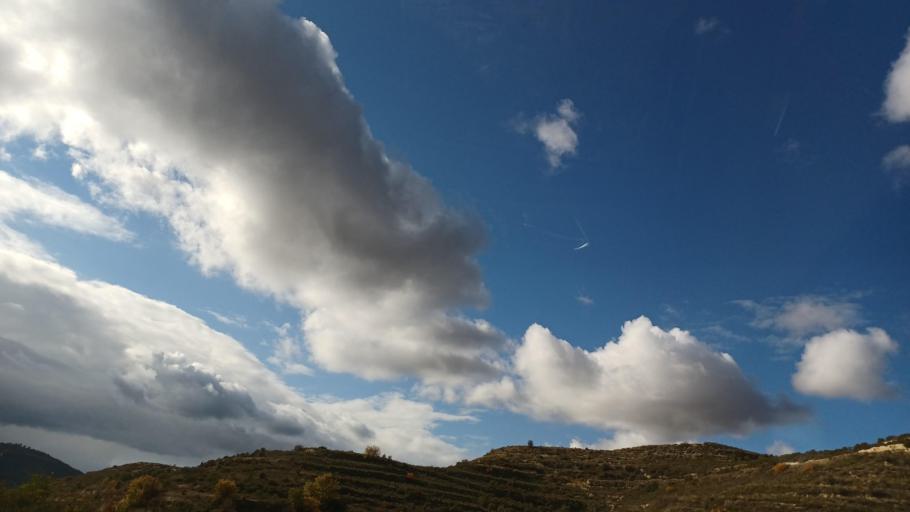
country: CY
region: Limassol
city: Pachna
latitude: 34.7859
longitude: 32.8245
